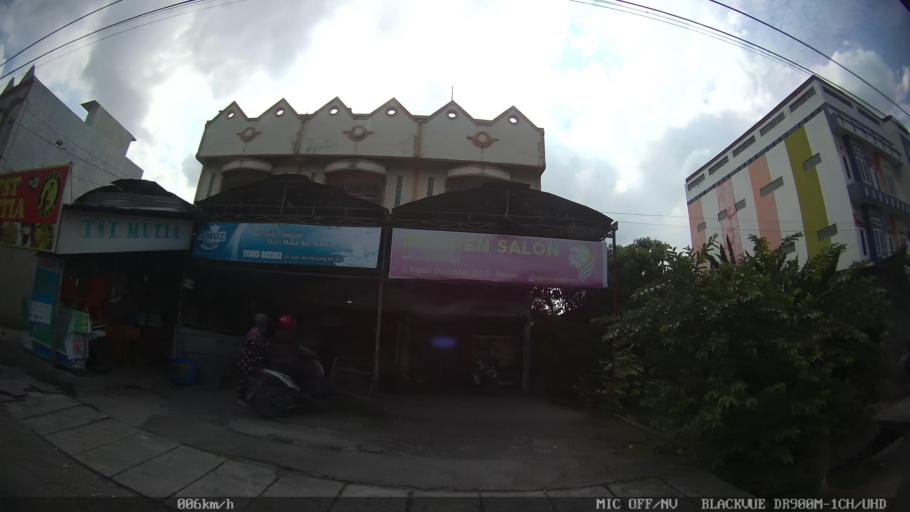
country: ID
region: North Sumatra
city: Medan
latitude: 3.6110
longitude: 98.6451
